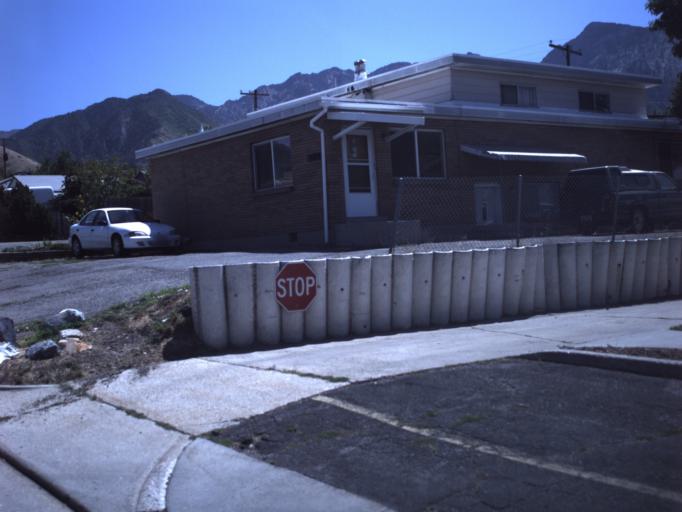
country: US
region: Utah
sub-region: Salt Lake County
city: East Millcreek
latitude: 40.6998
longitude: -111.8124
